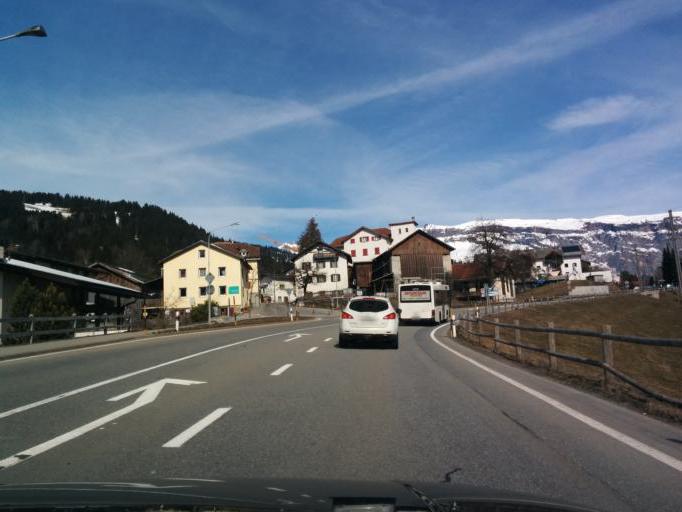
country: CH
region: Grisons
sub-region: Surselva District
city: Laax
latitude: 46.8019
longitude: 9.2561
